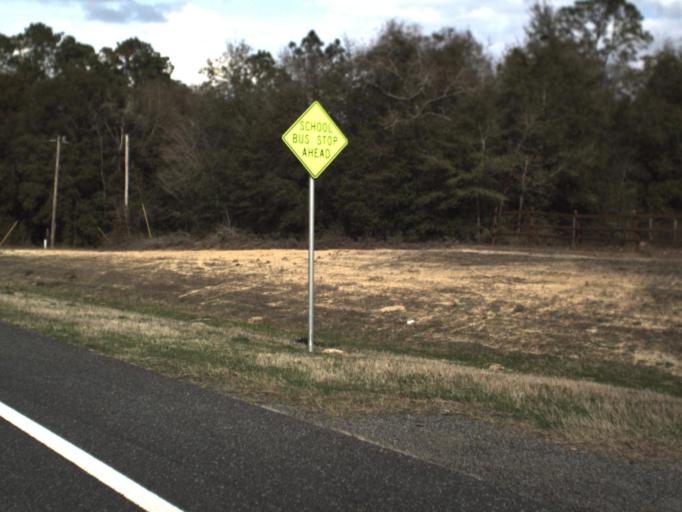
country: US
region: Florida
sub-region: Bay County
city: Youngstown
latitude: 30.5198
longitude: -85.4083
